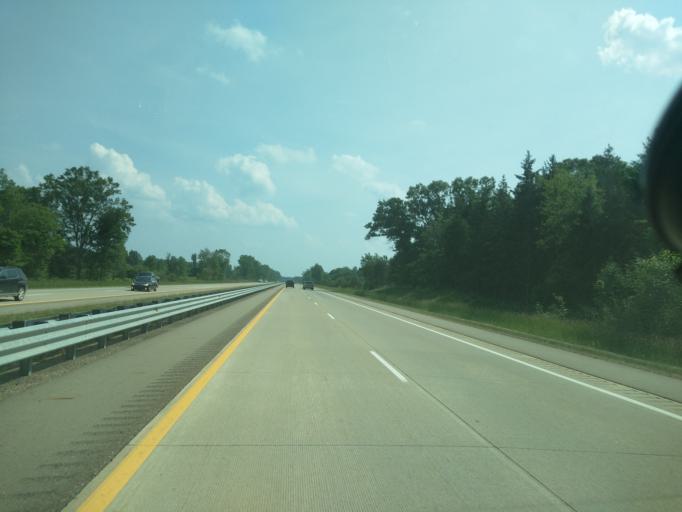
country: US
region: Michigan
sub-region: Jackson County
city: Jackson
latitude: 42.3432
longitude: -84.4290
